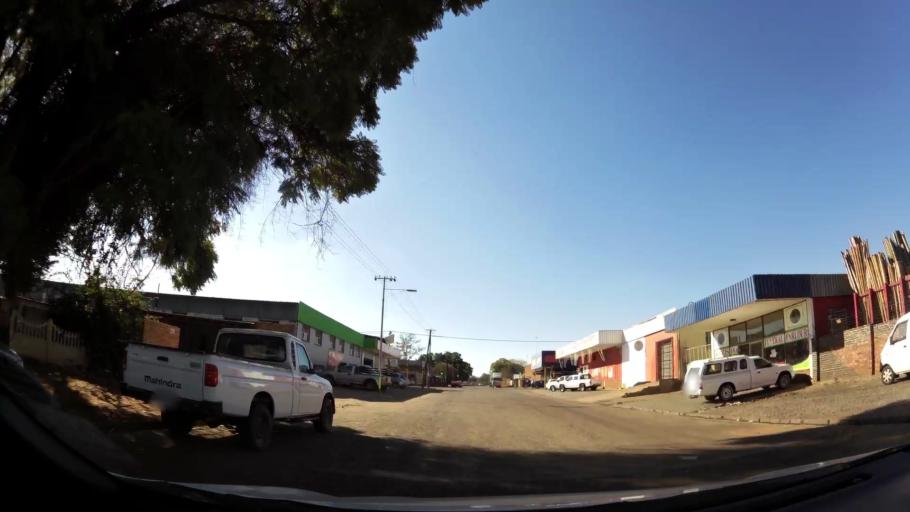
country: ZA
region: Limpopo
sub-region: Waterberg District Municipality
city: Mokopane
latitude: -24.1789
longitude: 29.0056
